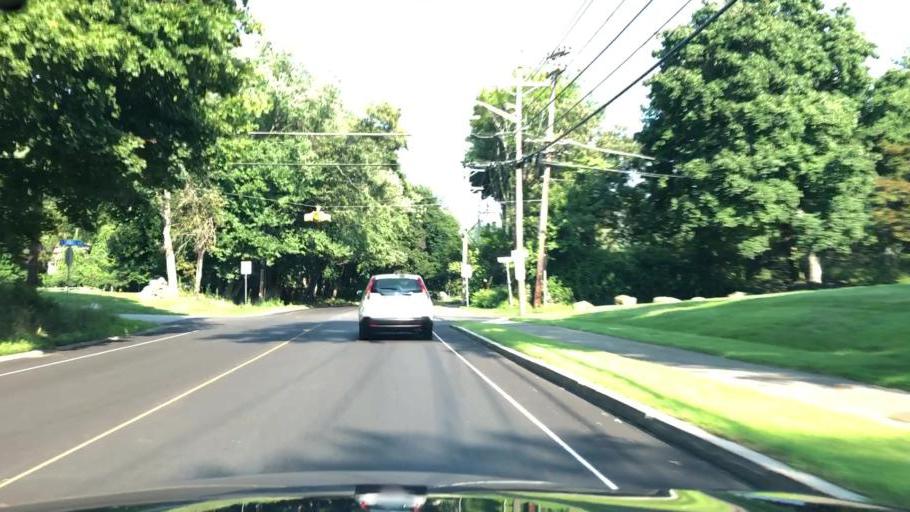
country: US
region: Massachusetts
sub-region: Middlesex County
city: Tewksbury
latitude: 42.6438
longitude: -71.2570
